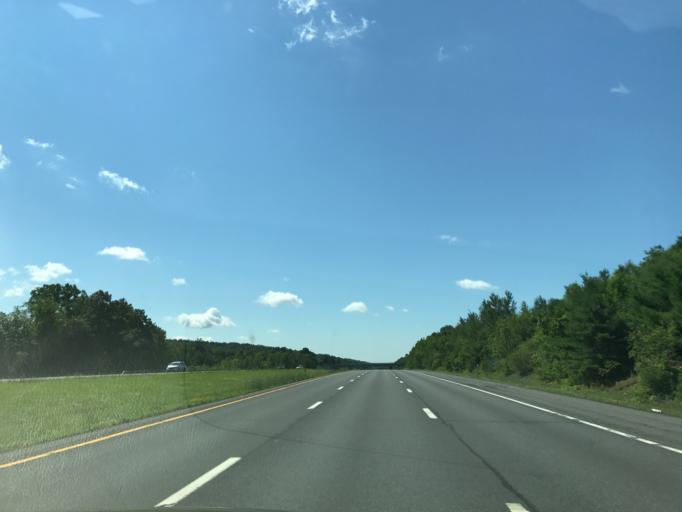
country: US
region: New York
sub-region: Rensselaer County
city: East Greenbush
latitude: 42.6055
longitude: -73.6843
